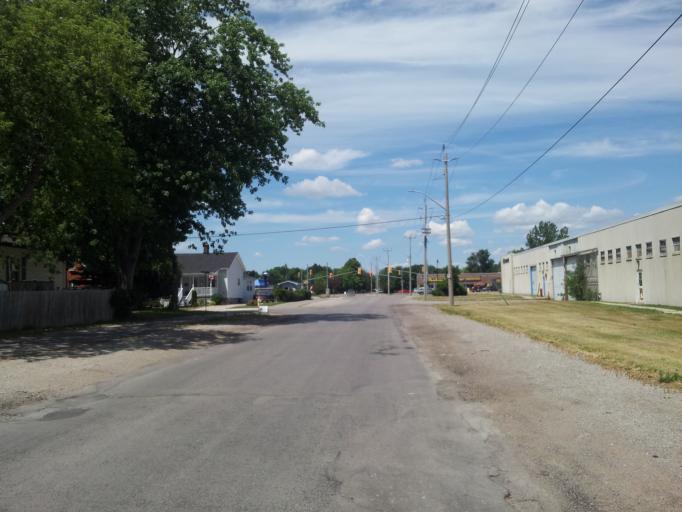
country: CA
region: Ontario
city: Stratford
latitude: 43.3695
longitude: -80.9578
